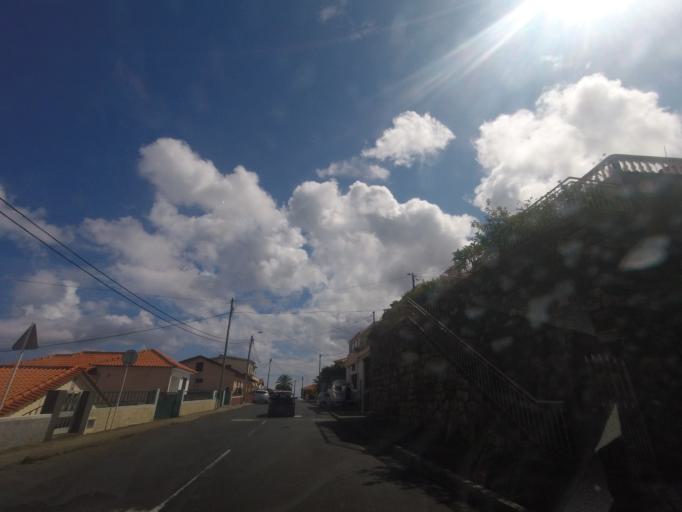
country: PT
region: Madeira
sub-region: Machico
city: Canical
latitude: 32.7433
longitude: -16.7400
